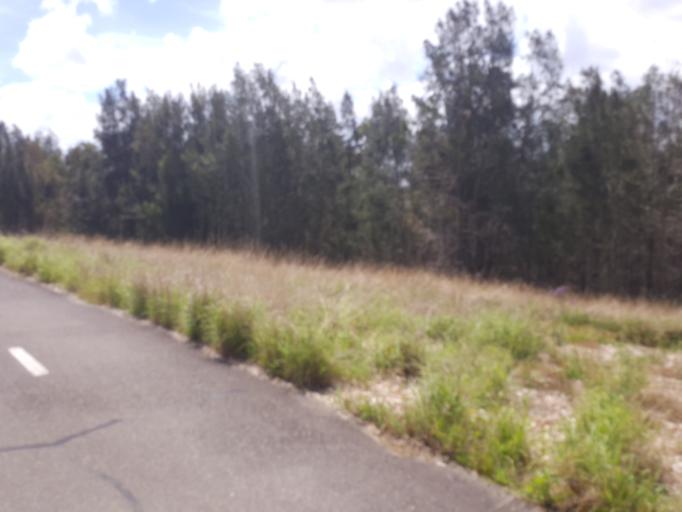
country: AU
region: New South Wales
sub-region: Canada Bay
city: Rhodes
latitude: -33.8262
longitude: 151.0730
